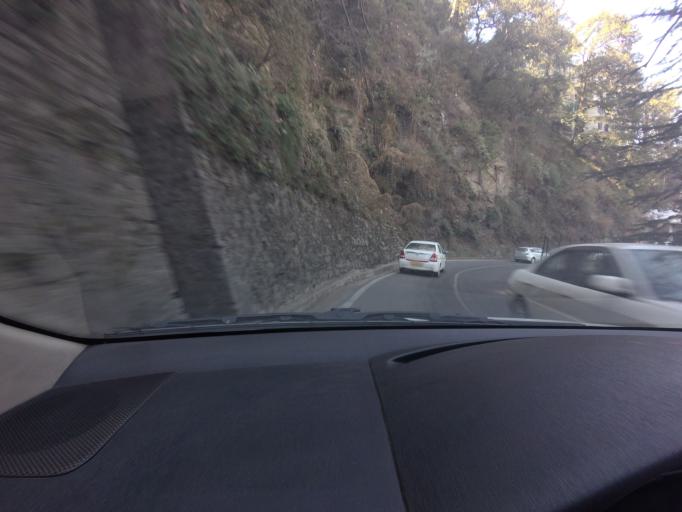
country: IN
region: Himachal Pradesh
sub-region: Shimla
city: Shimla
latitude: 31.1081
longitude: 77.1686
